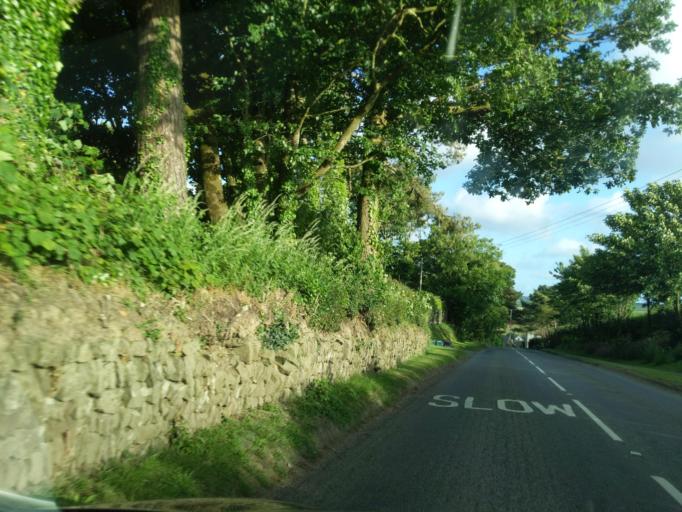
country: GB
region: England
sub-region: Devon
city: Fremington
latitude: 51.0263
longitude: -4.1014
